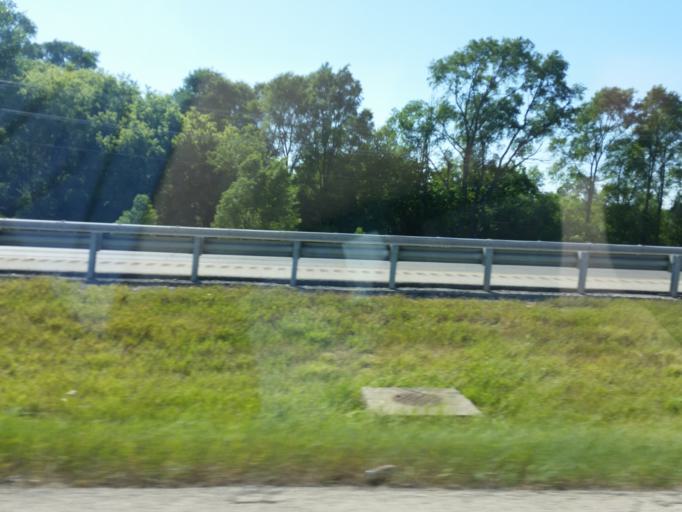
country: US
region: Illinois
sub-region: Winnebago County
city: Roscoe
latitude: 42.3902
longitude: -89.0169
